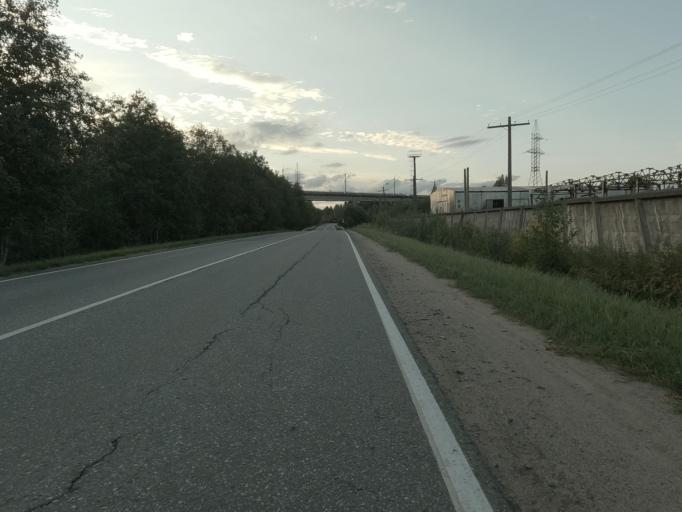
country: RU
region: Leningrad
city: Mga
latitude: 59.7572
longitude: 31.0202
